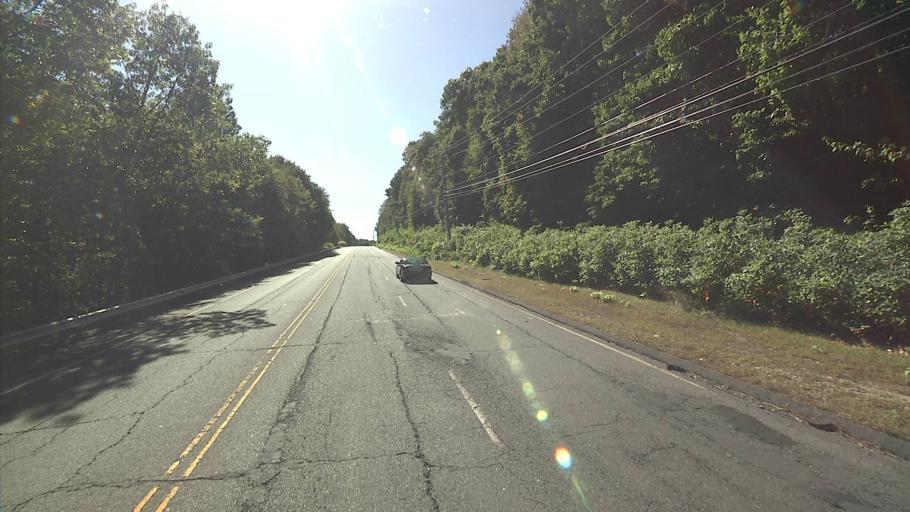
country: US
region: Connecticut
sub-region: Hartford County
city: Bristol
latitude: 41.6528
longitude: -72.9668
